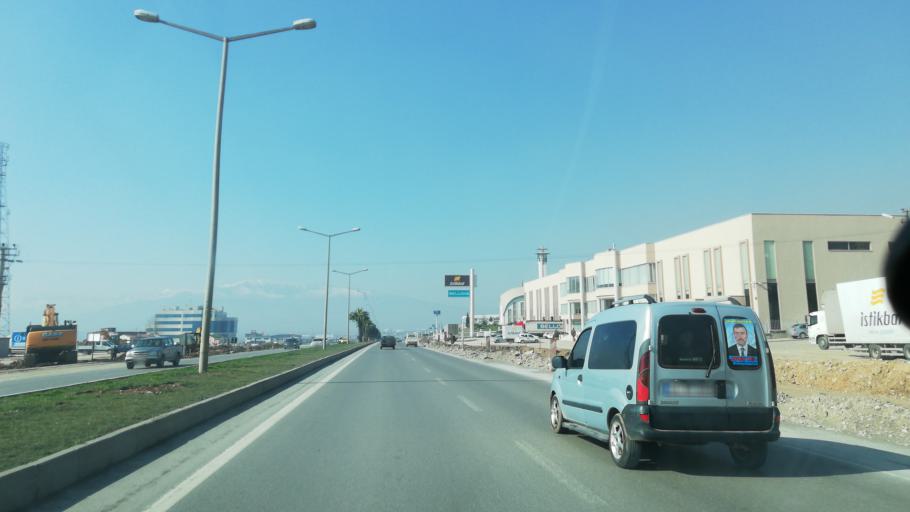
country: TR
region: Kahramanmaras
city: Kahramanmaras
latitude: 37.5685
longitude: 36.9118
